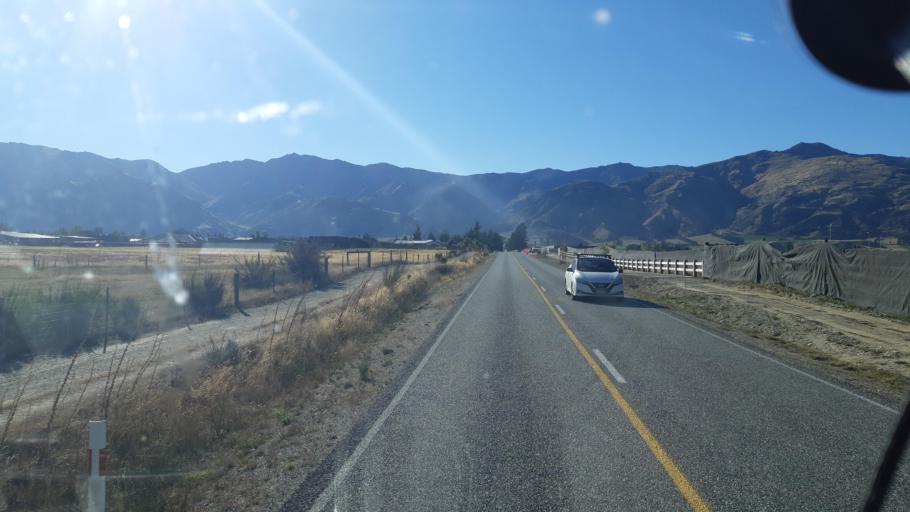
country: NZ
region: Otago
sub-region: Queenstown-Lakes District
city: Wanaka
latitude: -44.6185
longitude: 169.2640
